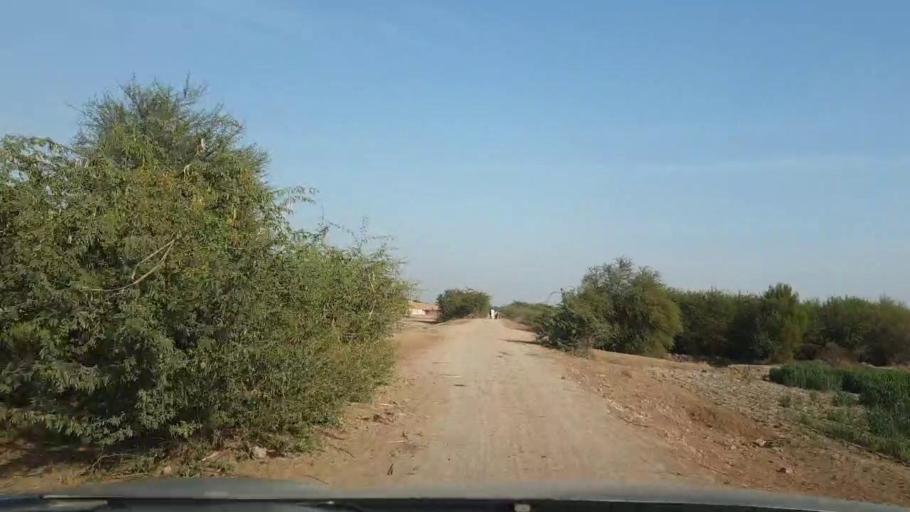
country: PK
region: Sindh
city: Berani
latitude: 25.7270
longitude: 68.7861
